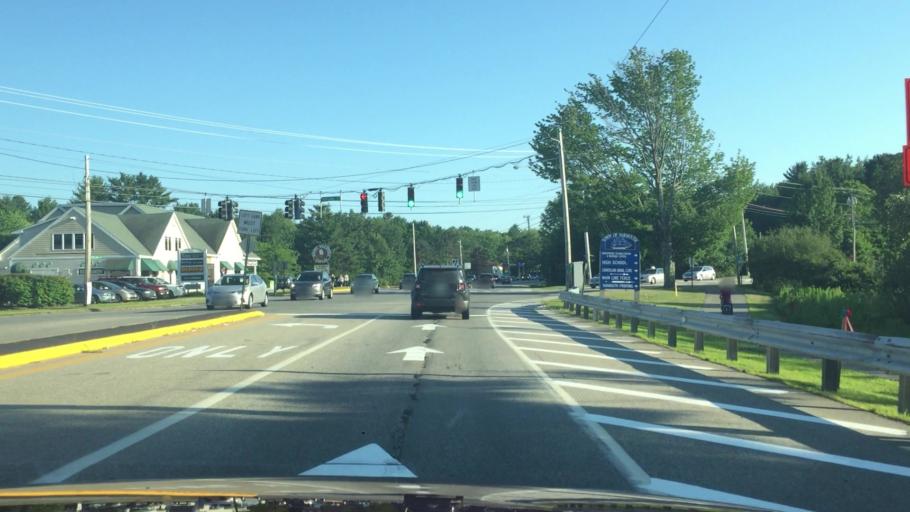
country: US
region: Maine
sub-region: Cumberland County
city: Yarmouth
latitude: 43.7931
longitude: -70.1887
